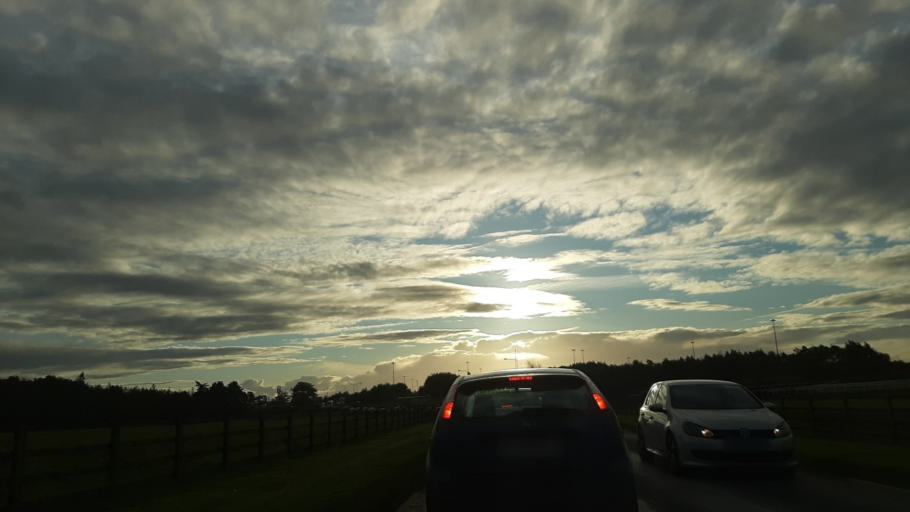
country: IE
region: Leinster
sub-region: Kildare
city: Athgarvan
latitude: 53.1641
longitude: -6.8311
